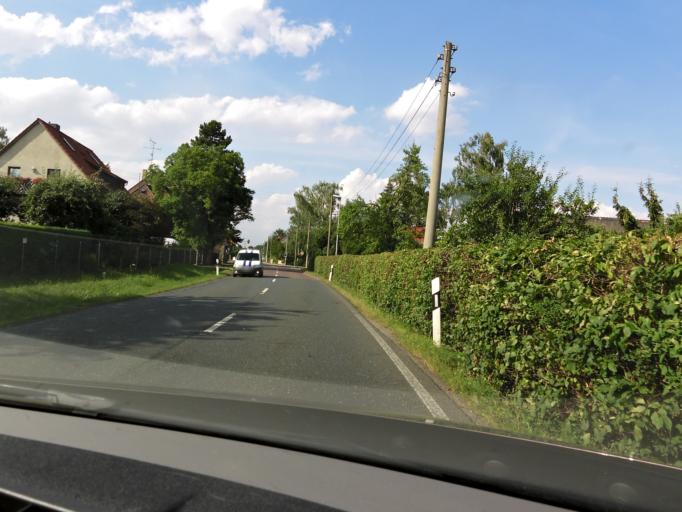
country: DE
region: Saxony
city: Grossposna
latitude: 51.3224
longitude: 12.4803
